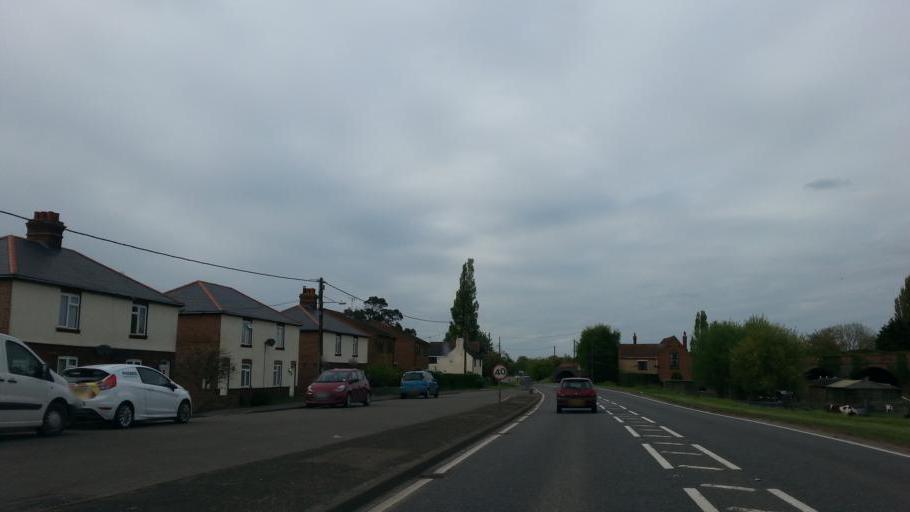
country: GB
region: England
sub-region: Cambridgeshire
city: March
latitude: 52.6015
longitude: 0.0629
